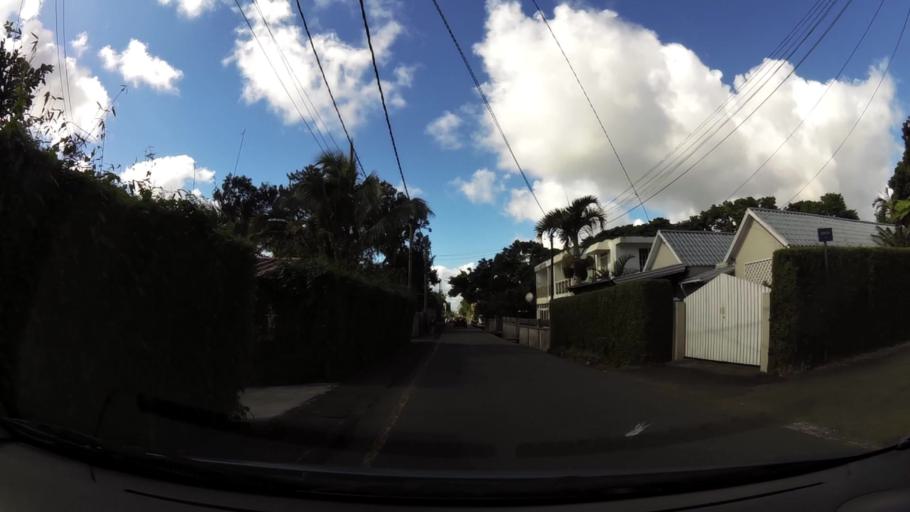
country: MU
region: Plaines Wilhems
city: Curepipe
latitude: -20.3256
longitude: 57.5311
